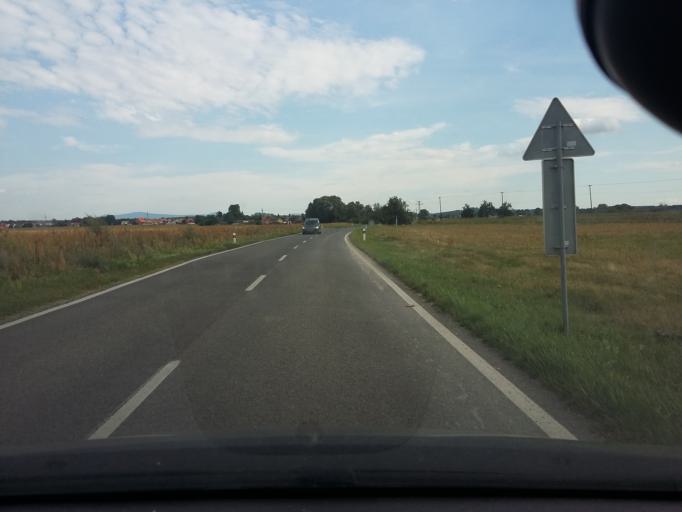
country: SK
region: Trnavsky
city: Gbely
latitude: 48.6414
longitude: 17.1959
